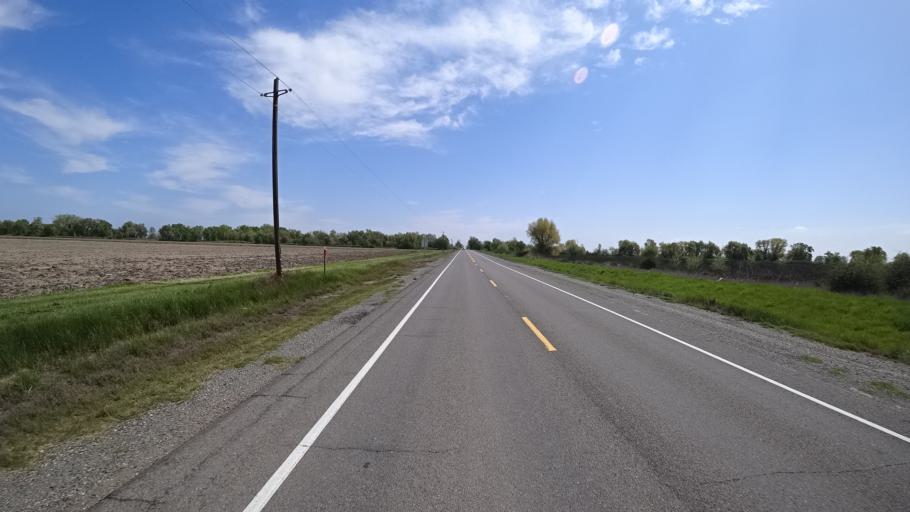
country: US
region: California
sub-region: Butte County
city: Biggs
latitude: 39.4641
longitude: -121.8744
